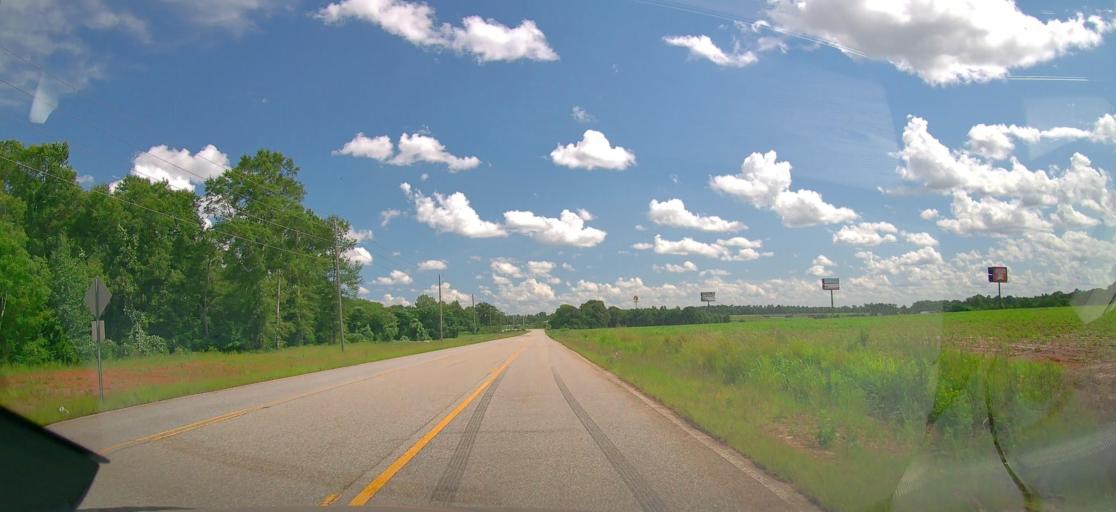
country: US
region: Georgia
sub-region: Houston County
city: Centerville
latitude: 32.5941
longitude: -83.7392
